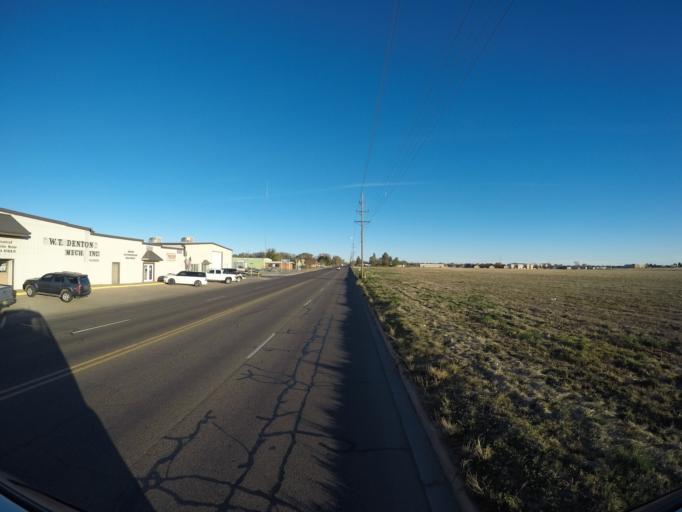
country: US
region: New Mexico
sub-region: Curry County
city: Clovis
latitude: 34.4013
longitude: -103.1788
